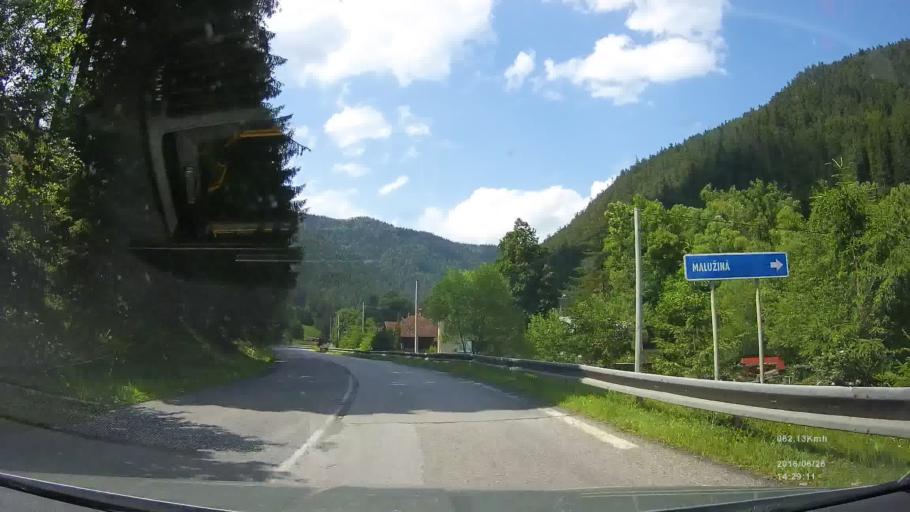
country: SK
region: Zilinsky
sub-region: Okres Zilina
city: Liptovsky Hradok
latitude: 48.9807
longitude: 19.7673
